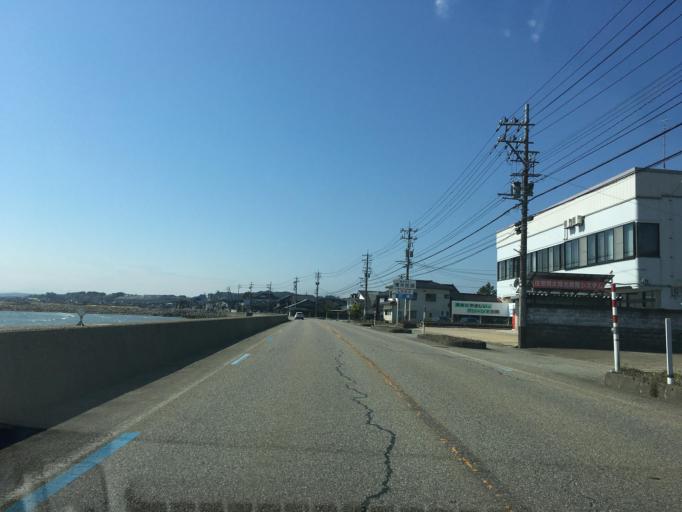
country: JP
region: Toyama
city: Himi
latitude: 36.8783
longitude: 136.9855
